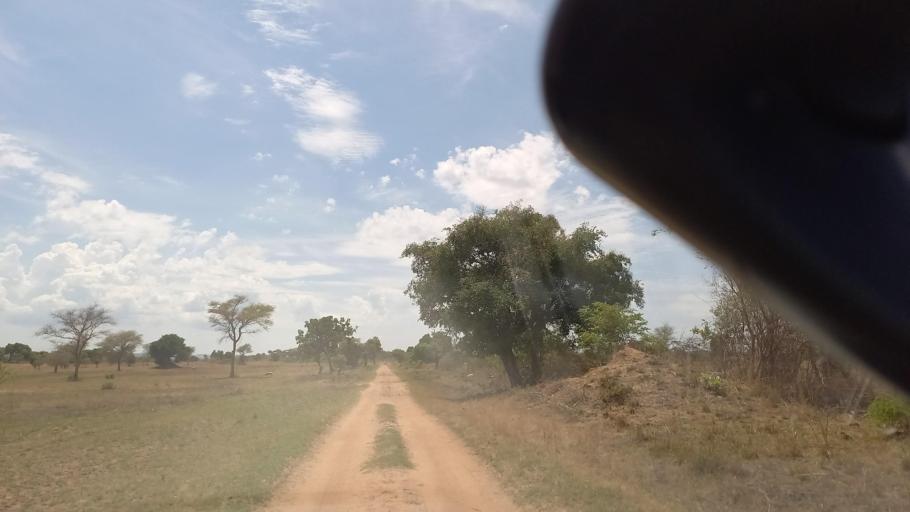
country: ZM
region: Southern
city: Mazabuka
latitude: -16.1441
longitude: 27.7706
